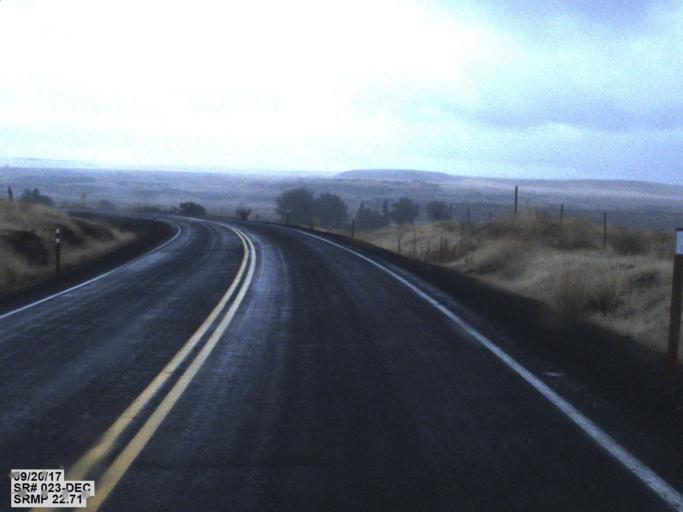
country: US
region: Washington
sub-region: Spokane County
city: Cheney
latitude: 47.1175
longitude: -117.7430
